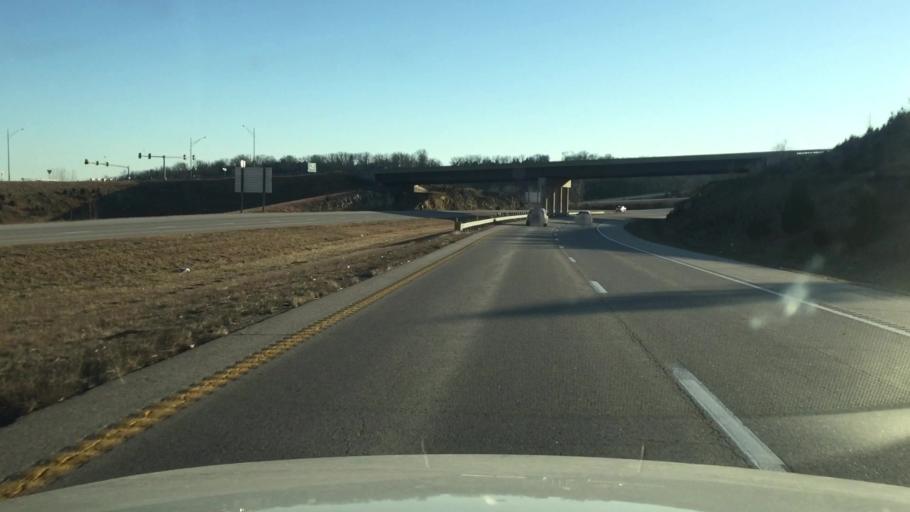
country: US
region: Missouri
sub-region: Cole County
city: Jefferson City
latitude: 38.5418
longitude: -92.2087
